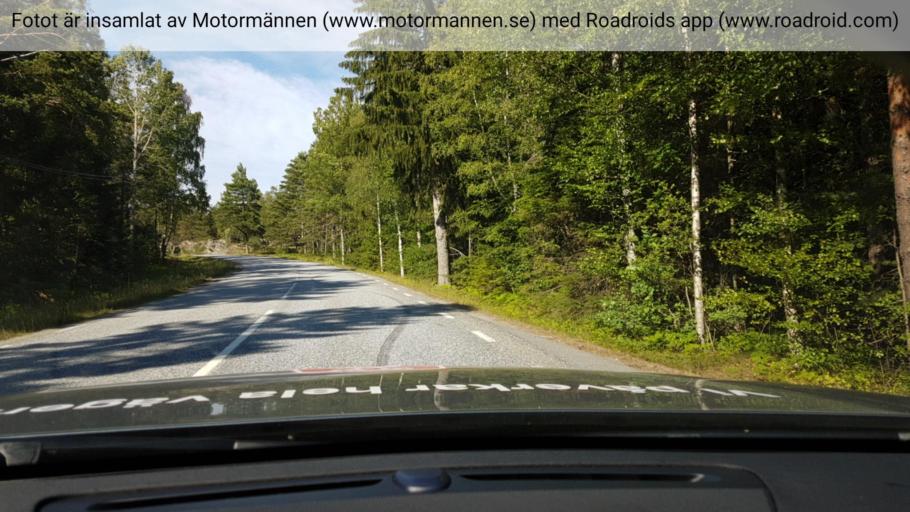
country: SE
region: Stockholm
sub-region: Haninge Kommun
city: Jordbro
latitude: 58.9905
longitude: 18.0995
